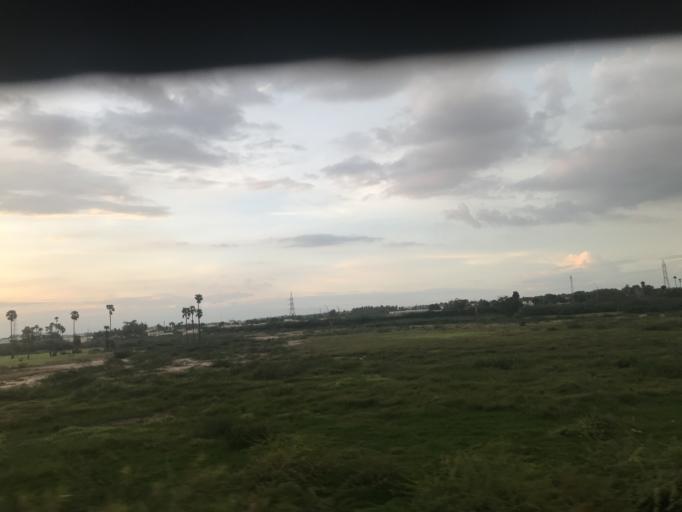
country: IN
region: Tamil Nadu
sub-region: Tiruppur
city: Tiruppur
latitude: 11.1343
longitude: 77.3738
